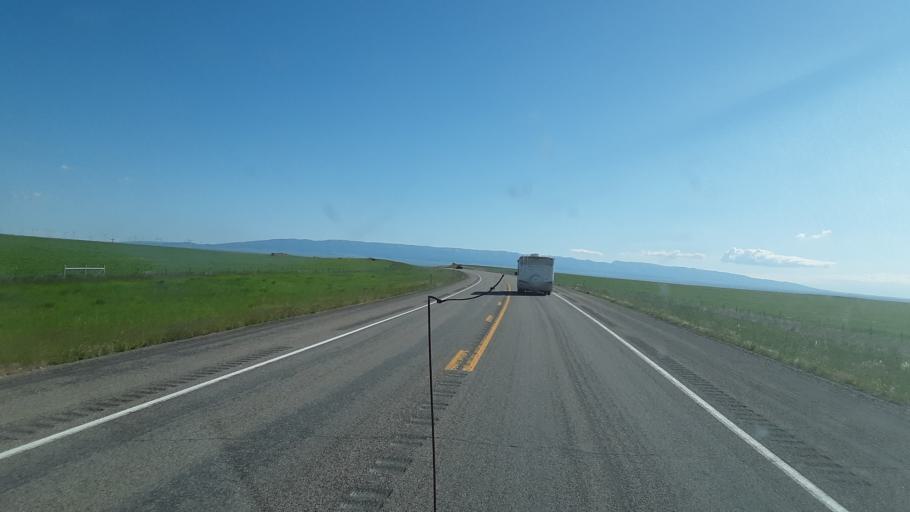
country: US
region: Montana
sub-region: Wheatland County
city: Harlowton
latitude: 46.4643
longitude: -109.7720
